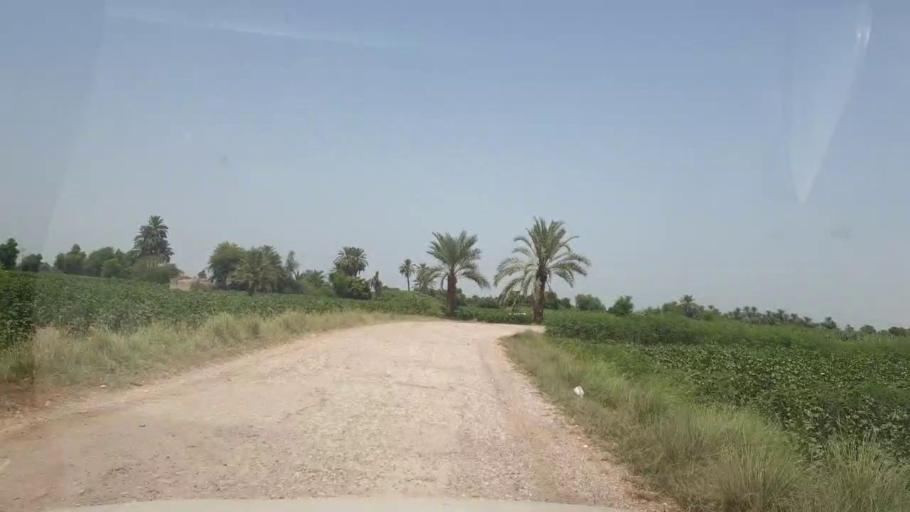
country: PK
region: Sindh
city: Bozdar
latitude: 27.1713
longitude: 68.6258
